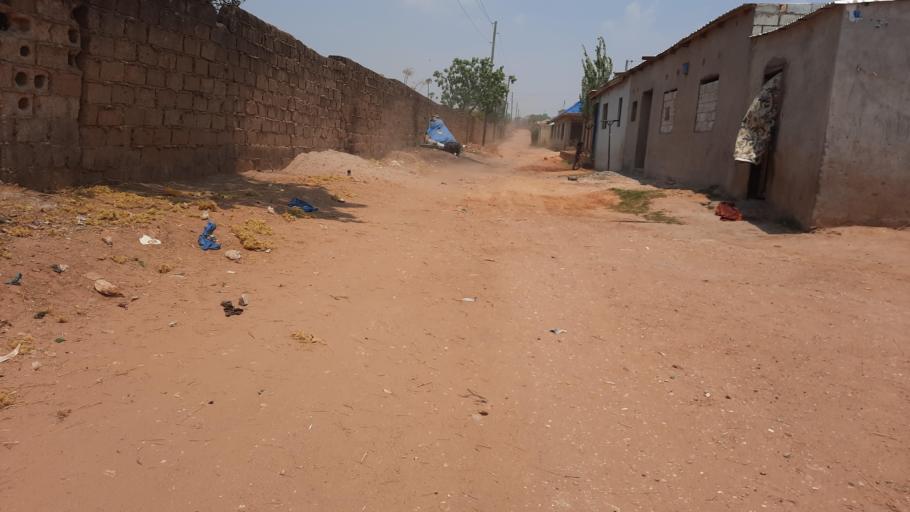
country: ZM
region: Lusaka
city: Lusaka
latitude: -15.4036
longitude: 28.3836
